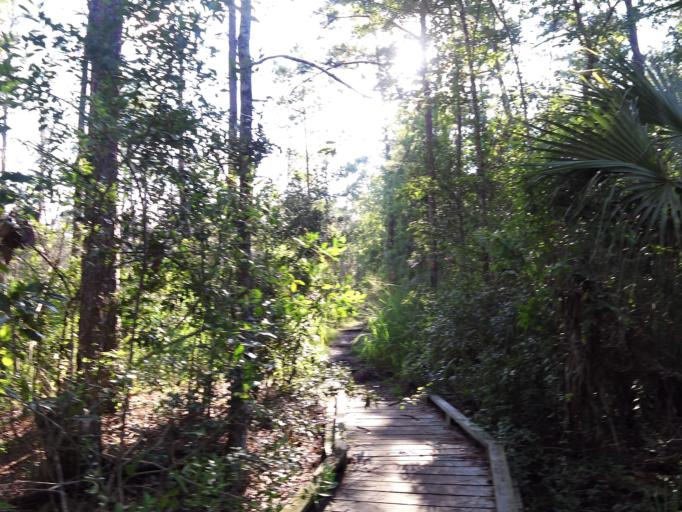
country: US
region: Florida
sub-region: Clay County
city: Bellair-Meadowbrook Terrace
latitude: 30.2438
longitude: -81.7007
